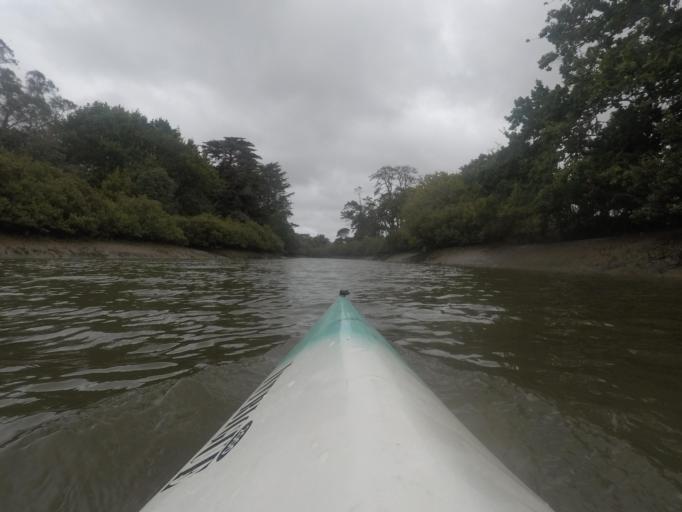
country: NZ
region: Auckland
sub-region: Auckland
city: Rosebank
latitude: -36.8604
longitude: 174.6387
